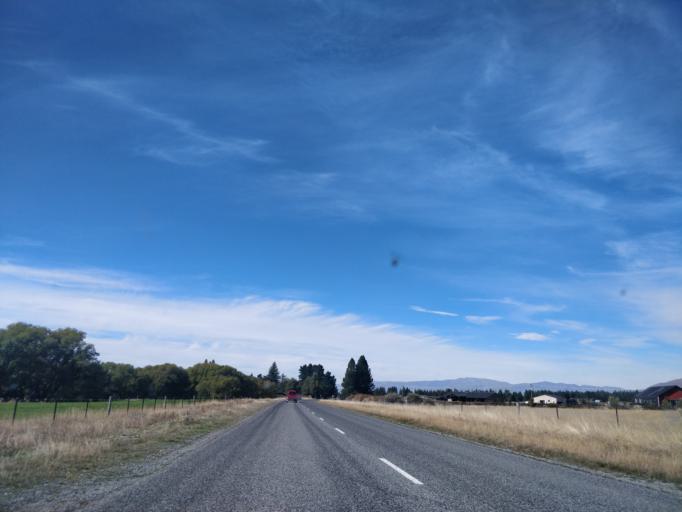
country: NZ
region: Otago
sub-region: Queenstown-Lakes District
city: Wanaka
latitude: -44.2380
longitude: 170.0782
